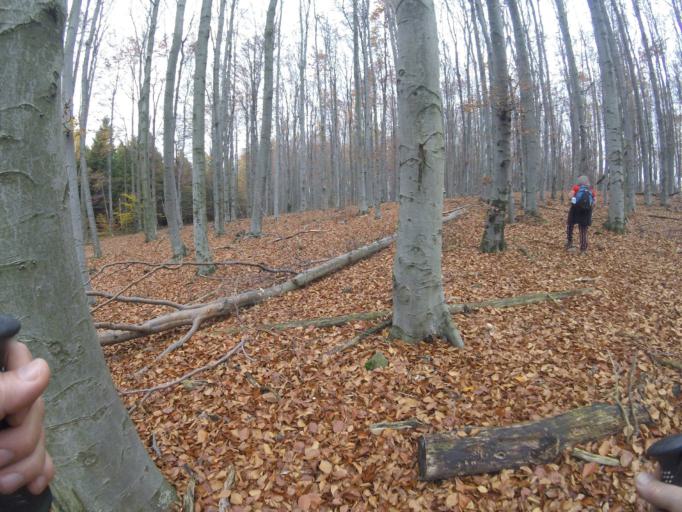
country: HU
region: Borsod-Abauj-Zemplen
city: Gonc
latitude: 48.4170
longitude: 21.3866
